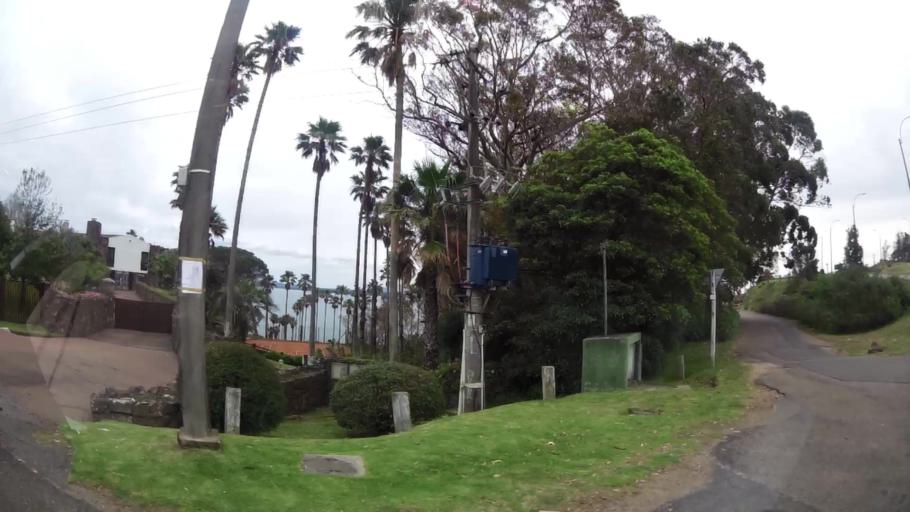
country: UY
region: Maldonado
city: Maldonado
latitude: -34.8973
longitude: -55.0380
